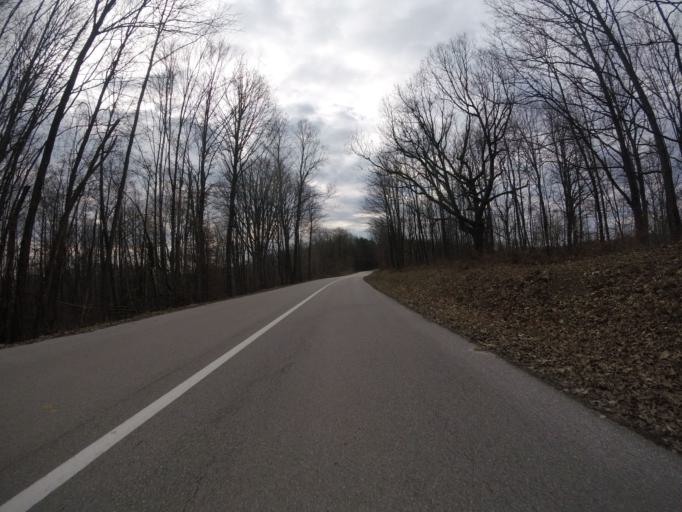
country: HR
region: Zagrebacka
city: Mraclin
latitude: 45.5376
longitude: 16.0585
